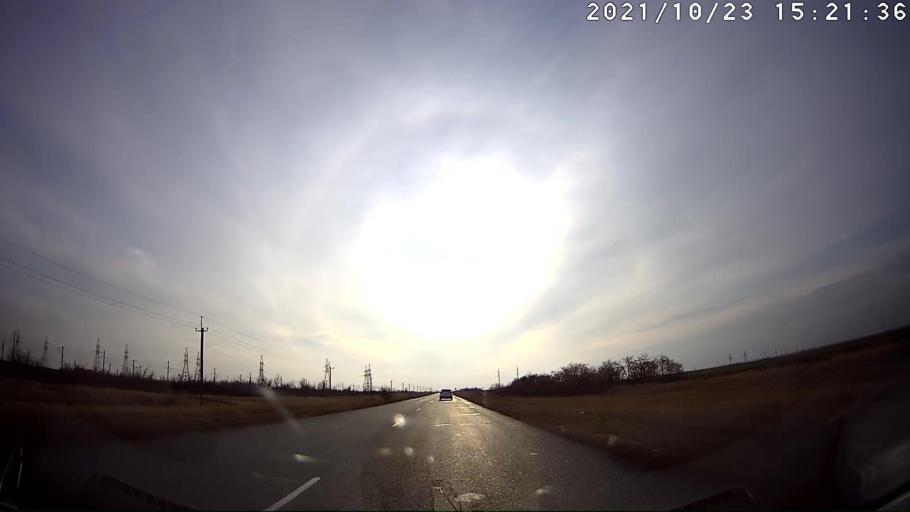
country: RU
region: Volgograd
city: Bereslavka
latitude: 48.3104
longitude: 44.3094
